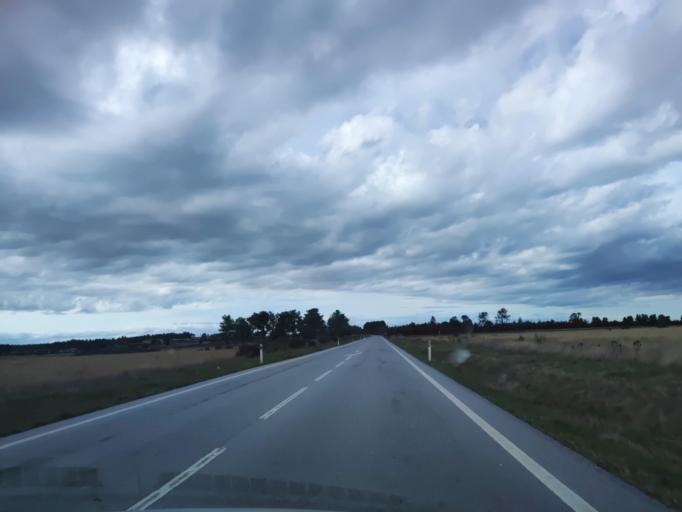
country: ES
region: Castille and Leon
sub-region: Provincia de Salamanca
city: Aldea del Obispo
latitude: 40.6652
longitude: -6.8581
